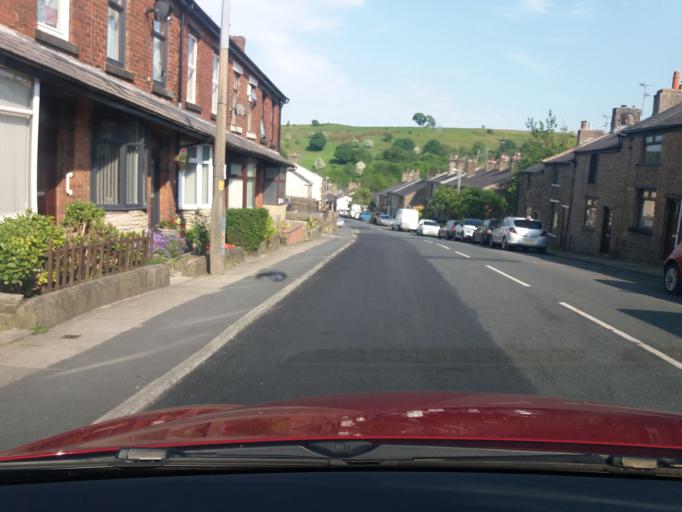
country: GB
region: England
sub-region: Lancashire
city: Chorley
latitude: 53.6881
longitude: -2.5685
